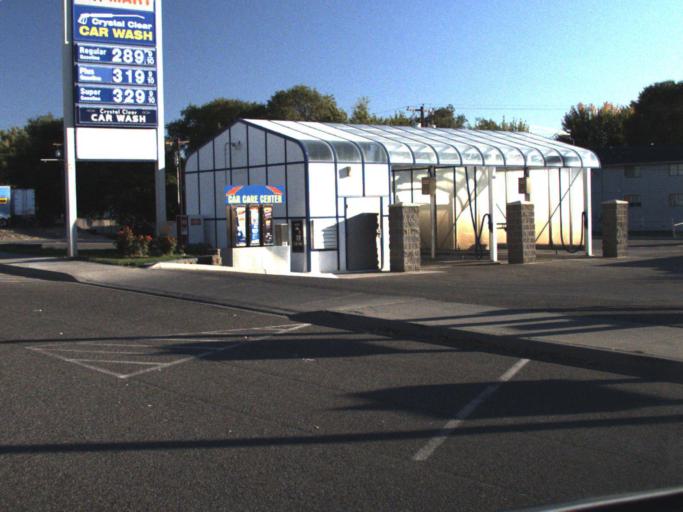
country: US
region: Washington
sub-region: Benton County
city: Benton City
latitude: 46.2657
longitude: -119.4876
